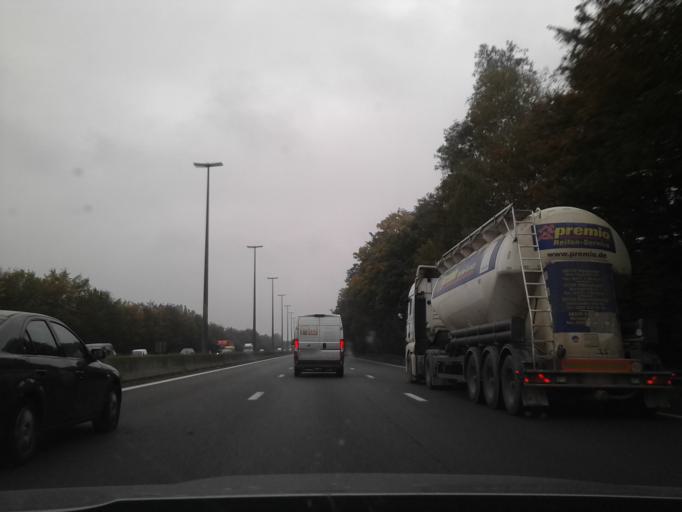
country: BE
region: Wallonia
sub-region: Province du Hainaut
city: Quaregnon
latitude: 50.4533
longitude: 3.8656
